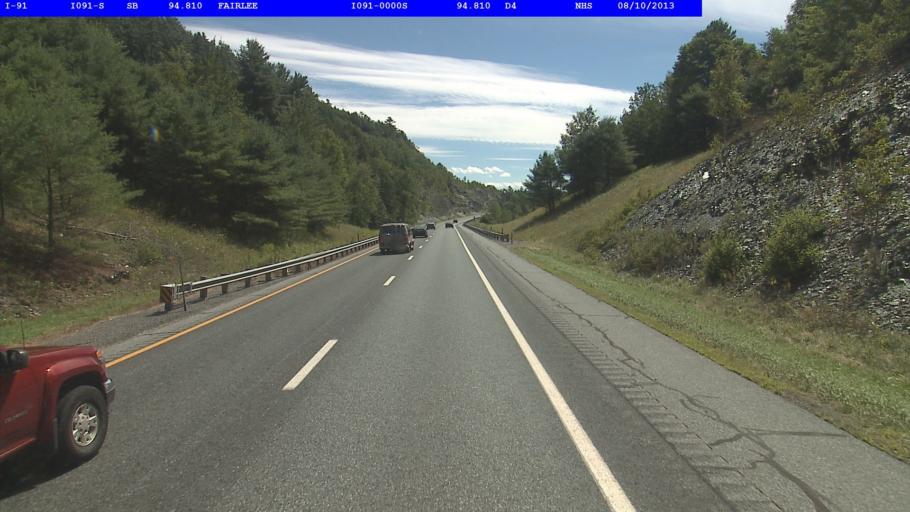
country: US
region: New Hampshire
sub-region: Grafton County
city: Orford
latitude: 43.9450
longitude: -72.1330
